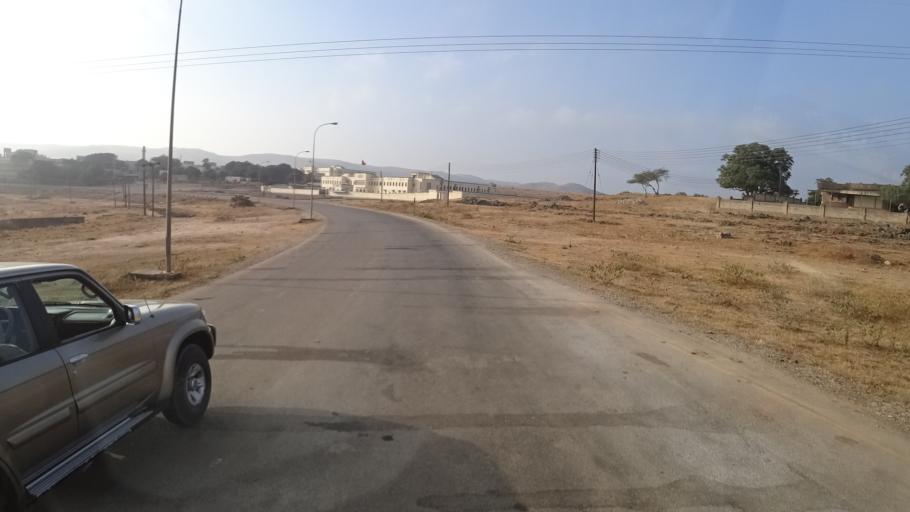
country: OM
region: Zufar
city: Salalah
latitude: 17.1249
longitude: 53.9985
